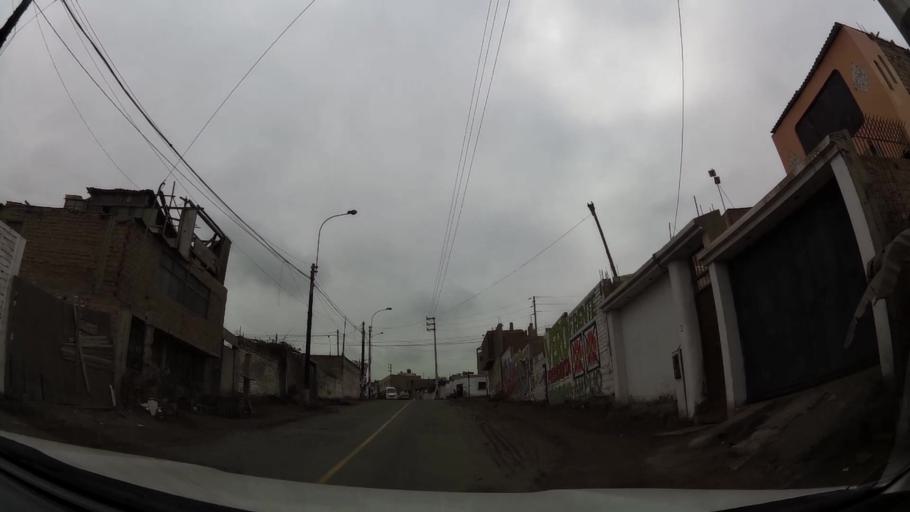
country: PE
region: Lima
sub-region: Lima
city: Surco
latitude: -12.2014
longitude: -76.9914
